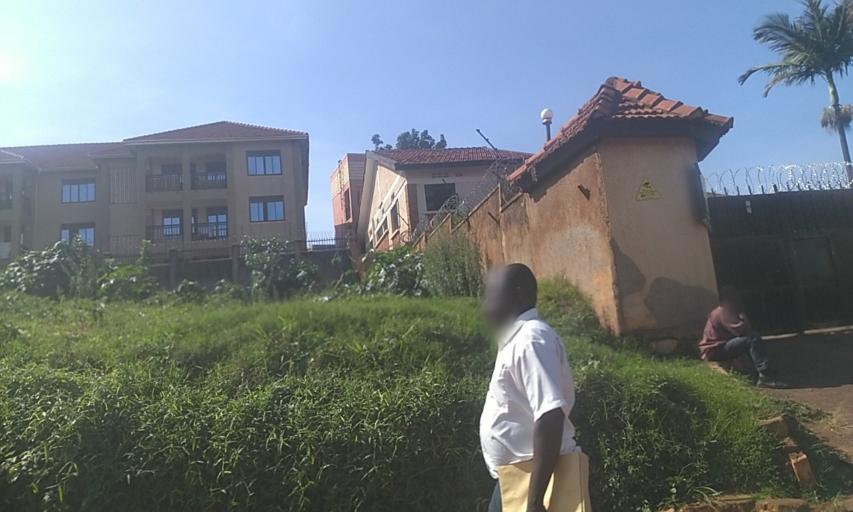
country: UG
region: Central Region
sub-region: Wakiso District
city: Kireka
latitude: 0.3601
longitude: 32.6179
